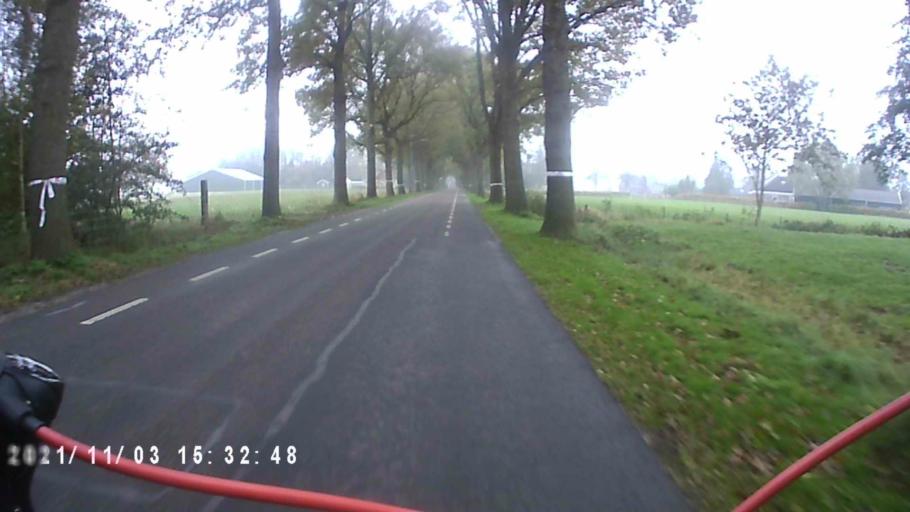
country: NL
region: Groningen
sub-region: Gemeente Leek
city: Leek
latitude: 53.1255
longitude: 6.3664
